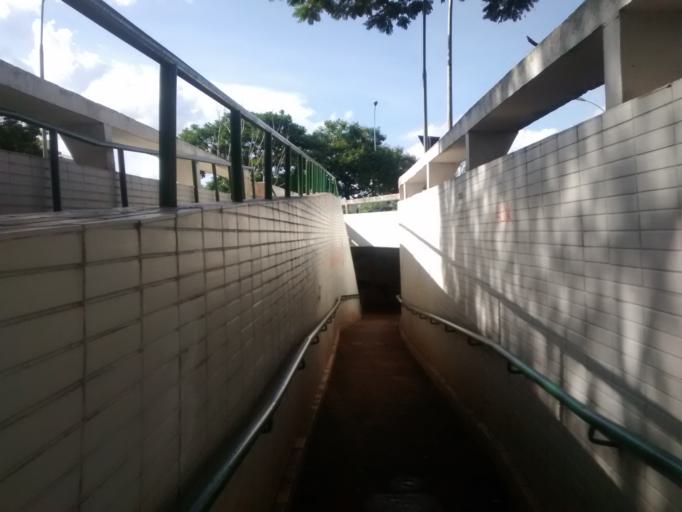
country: BR
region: Federal District
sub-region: Brasilia
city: Brasilia
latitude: -15.7468
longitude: -47.8899
